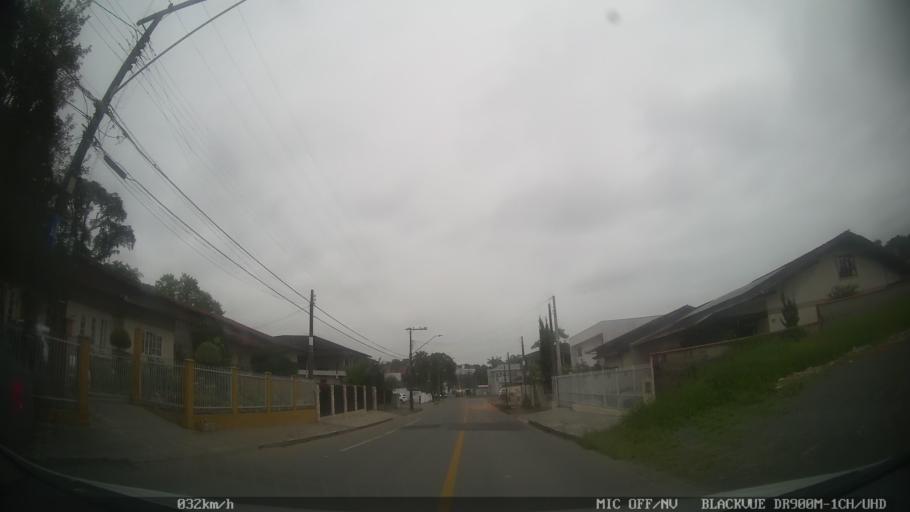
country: BR
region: Santa Catarina
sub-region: Joinville
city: Joinville
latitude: -26.3281
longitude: -48.8500
